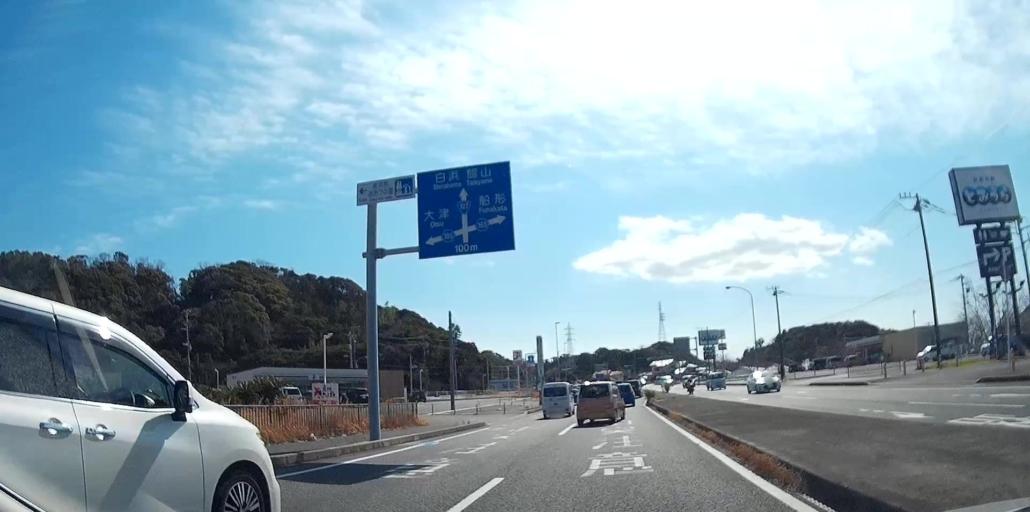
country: JP
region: Chiba
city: Tateyama
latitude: 35.0377
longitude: 139.8508
